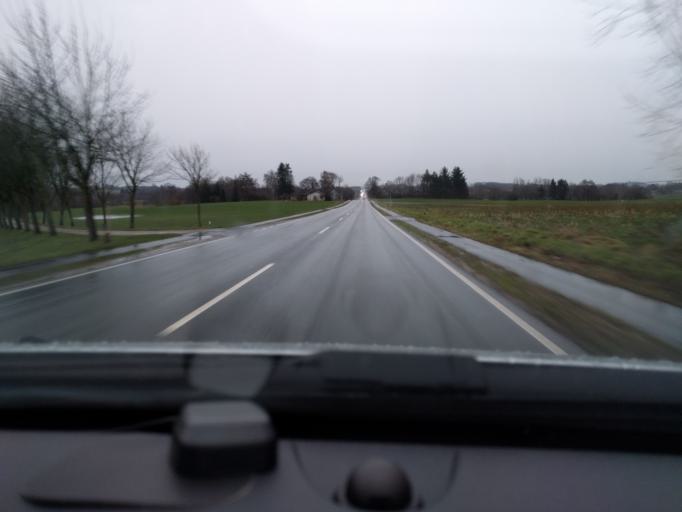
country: DK
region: Central Jutland
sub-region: Silkeborg Kommune
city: Silkeborg
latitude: 56.2198
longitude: 9.4949
